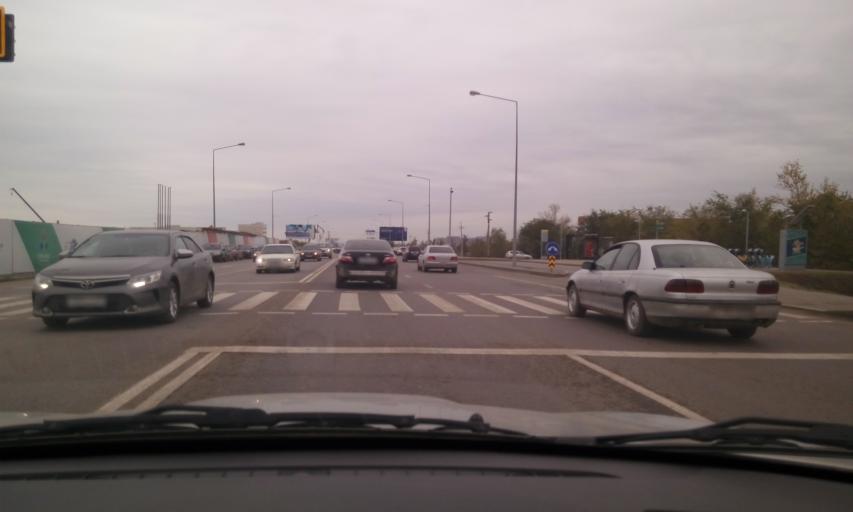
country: KZ
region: Astana Qalasy
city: Astana
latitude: 51.0897
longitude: 71.4027
